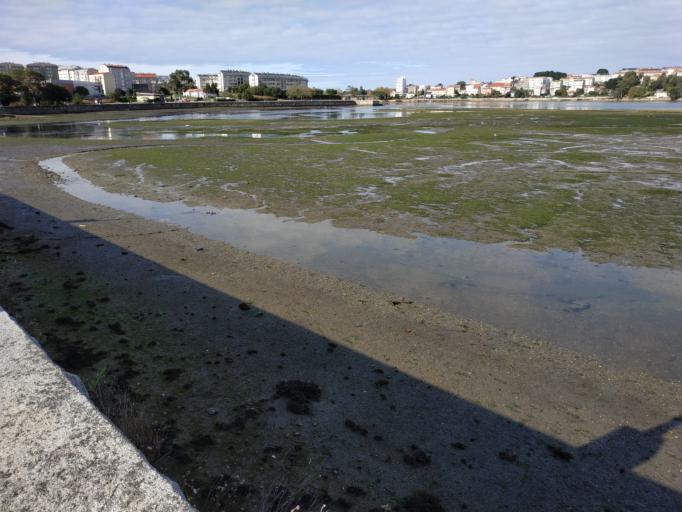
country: ES
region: Galicia
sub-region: Provincia da Coruna
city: Culleredo
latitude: 43.3242
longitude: -8.3781
